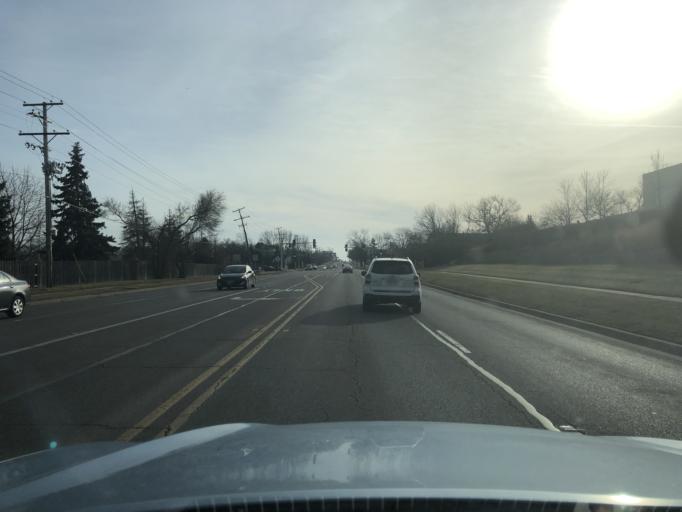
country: US
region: Illinois
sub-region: DuPage County
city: Glendale Heights
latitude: 41.9259
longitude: -88.0810
